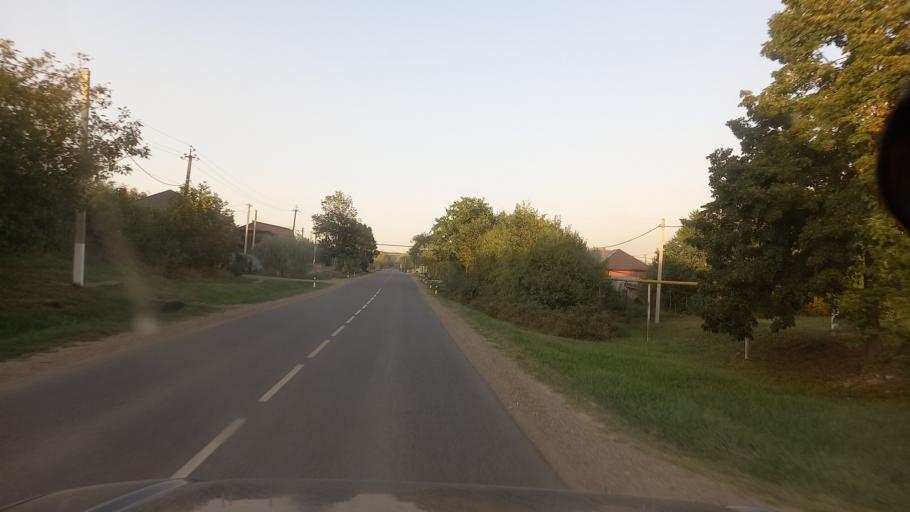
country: RU
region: Krasnodarskiy
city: Smolenskaya
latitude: 44.7713
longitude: 38.7836
